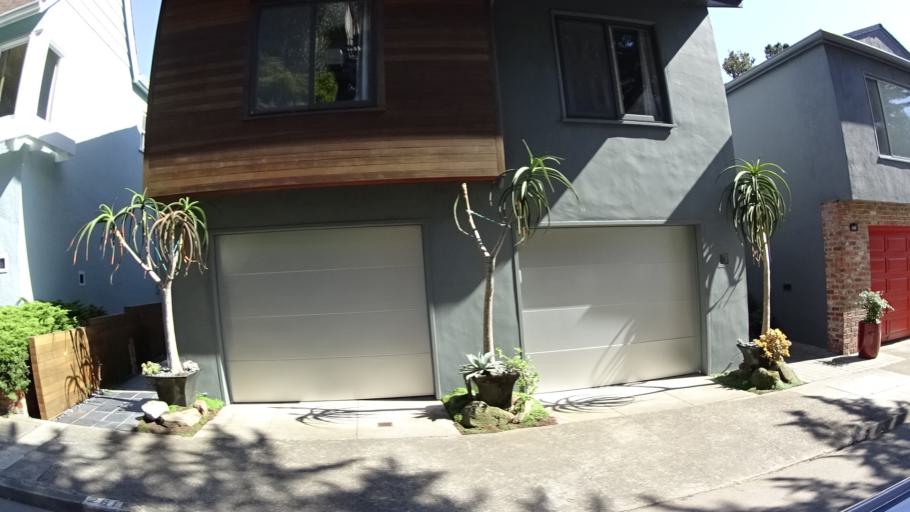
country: US
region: California
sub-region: San Francisco County
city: San Francisco
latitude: 37.7549
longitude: -122.4578
